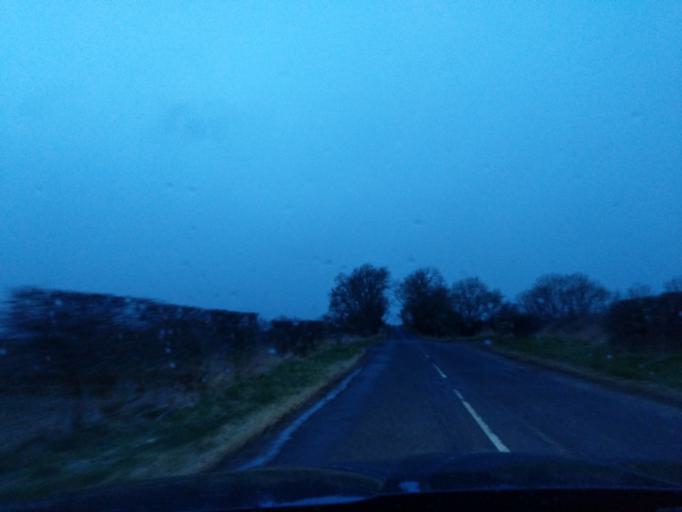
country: GB
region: England
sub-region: Northumberland
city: Ford
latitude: 55.7156
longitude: -2.1342
